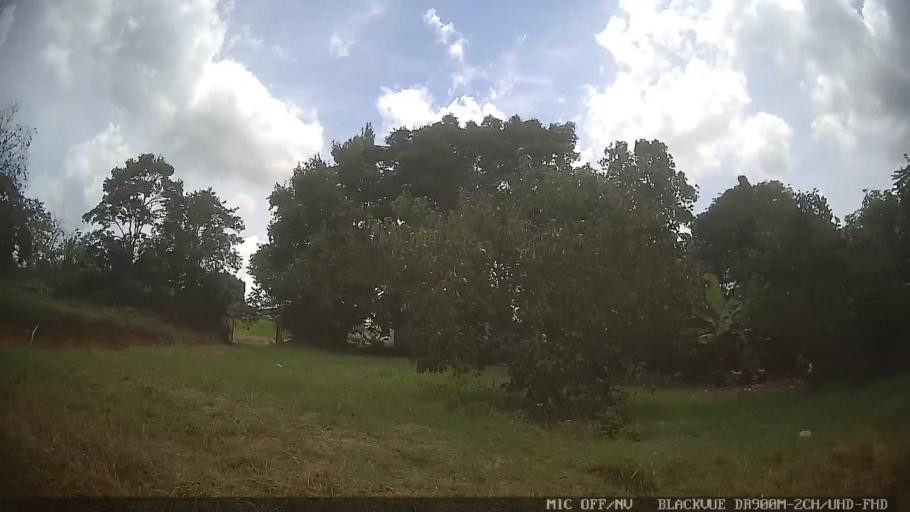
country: BR
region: Sao Paulo
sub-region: Atibaia
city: Atibaia
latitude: -23.0553
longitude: -46.5081
